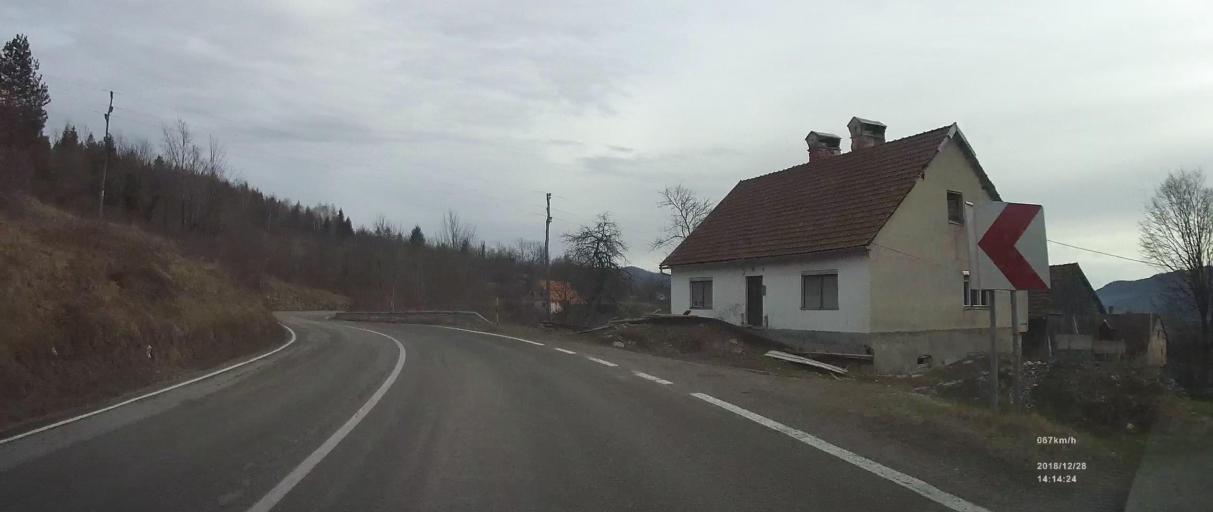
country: HR
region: Primorsko-Goranska
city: Vrbovsko
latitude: 45.4314
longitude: 15.0187
